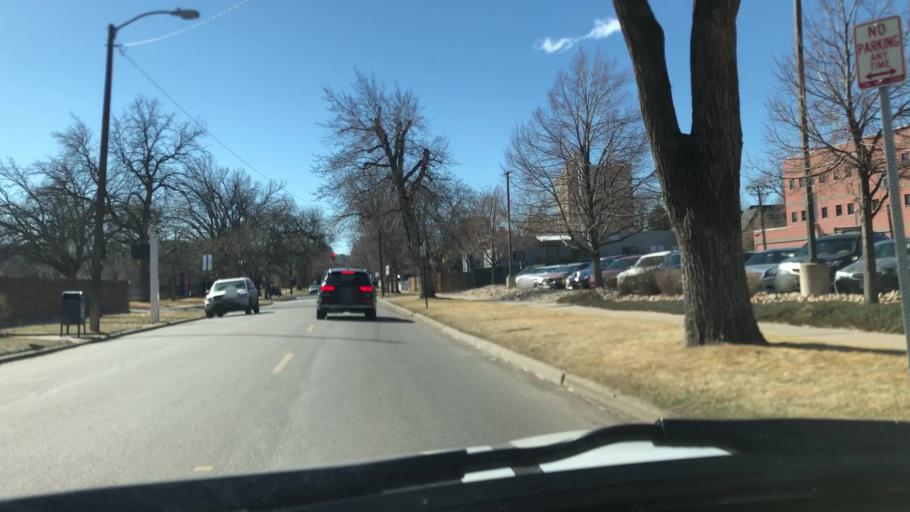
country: US
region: Colorado
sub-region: Denver County
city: Denver
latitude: 39.7460
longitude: -104.9648
